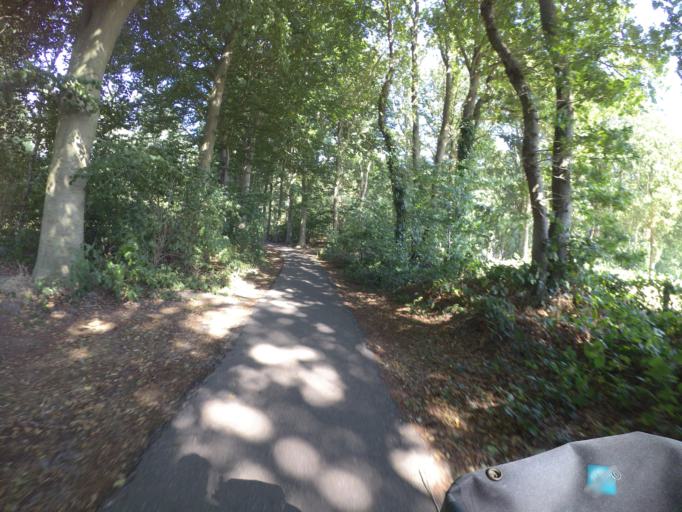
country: NL
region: Friesland
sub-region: Gemeente Gaasterlan-Sleat
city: Balk
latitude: 52.8690
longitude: 5.5717
